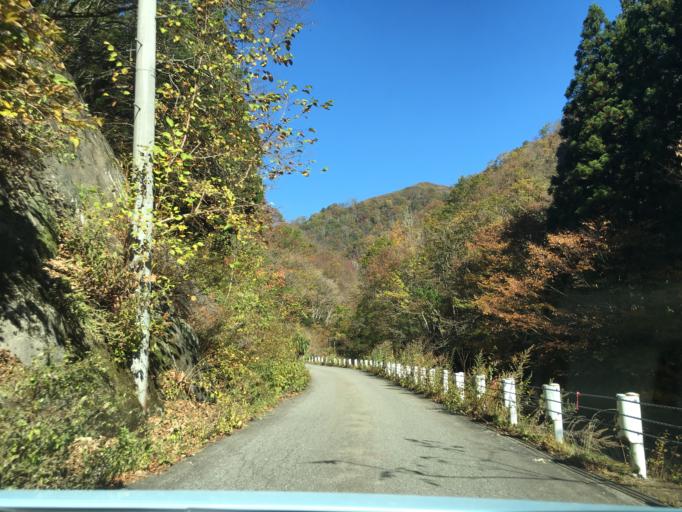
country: JP
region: Fukushima
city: Inawashiro
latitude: 37.4216
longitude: 139.9870
